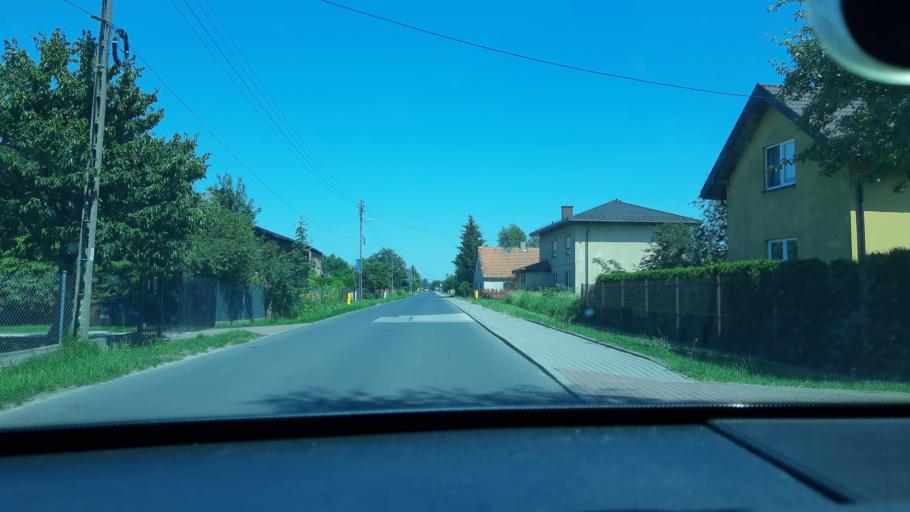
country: PL
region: Lodz Voivodeship
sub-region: Powiat zdunskowolski
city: Zdunska Wola
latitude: 51.6201
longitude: 18.9390
